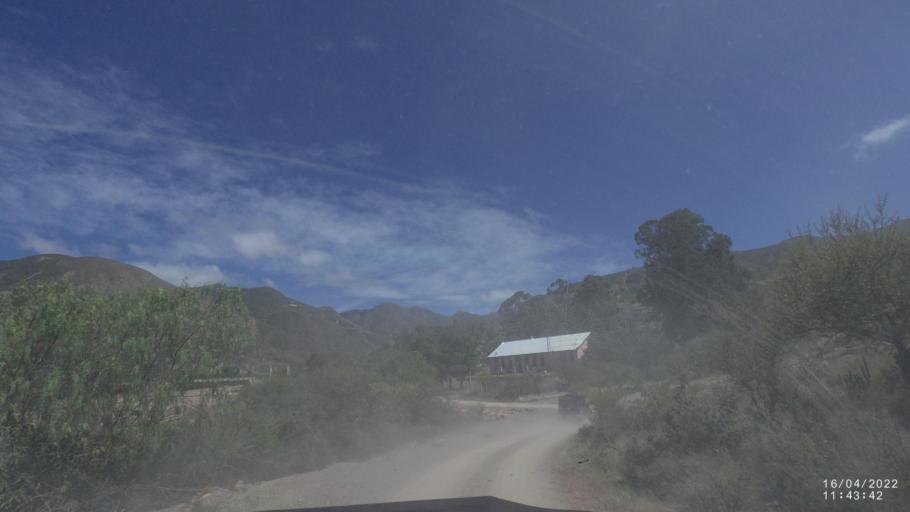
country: BO
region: Cochabamba
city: Mizque
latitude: -17.9821
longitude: -65.6301
